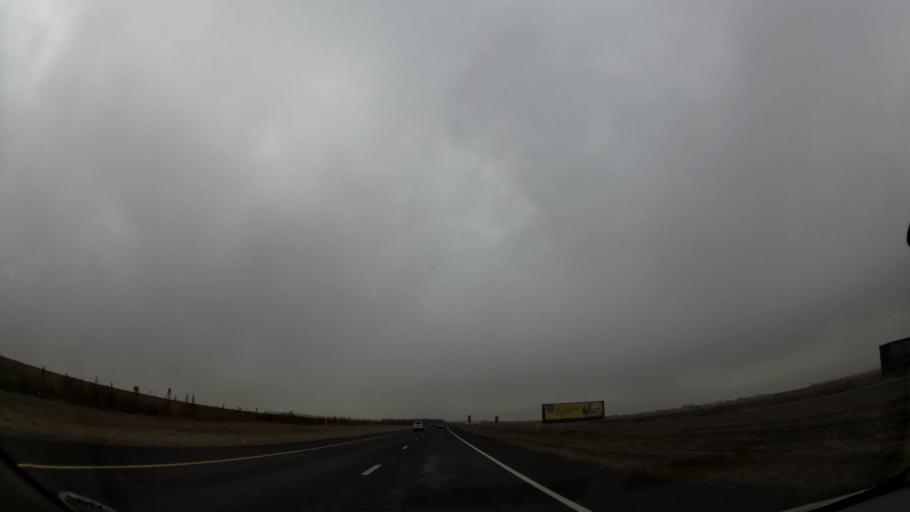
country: ZA
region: Mpumalanga
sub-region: Nkangala District Municipality
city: Delmas
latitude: -26.0719
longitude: 28.7457
